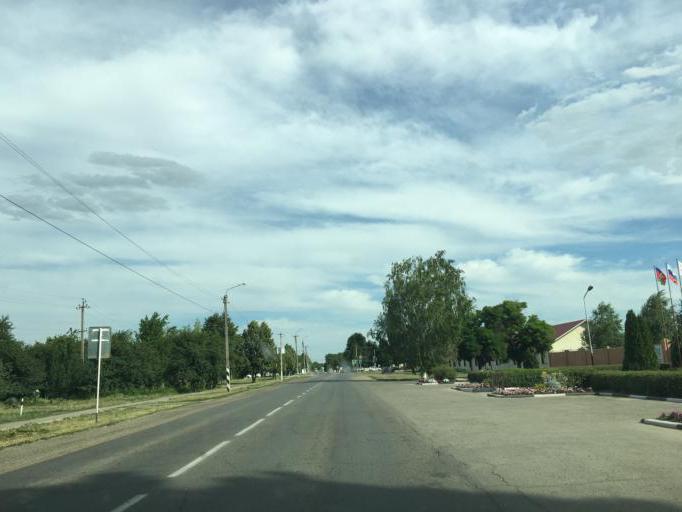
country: RU
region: Krasnodarskiy
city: Kushchevskaya
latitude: 46.5487
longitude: 39.6175
